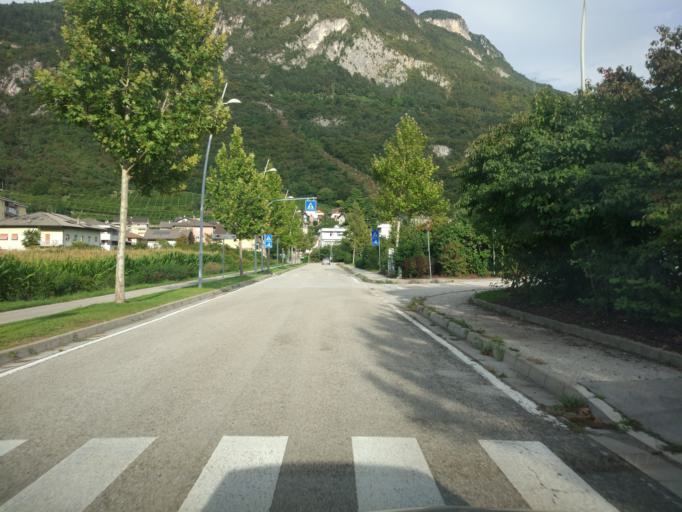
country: IT
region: Trentino-Alto Adige
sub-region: Provincia di Trento
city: Meano
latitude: 46.0988
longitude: 11.1159
